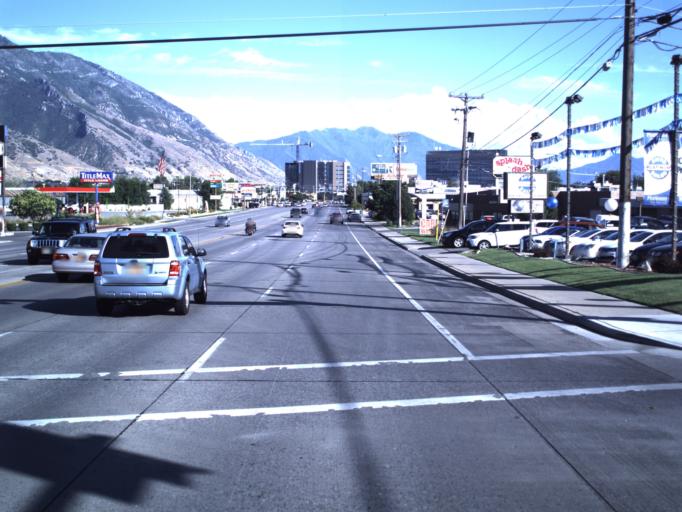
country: US
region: Utah
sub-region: Utah County
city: Provo
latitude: 40.2564
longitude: -111.6726
